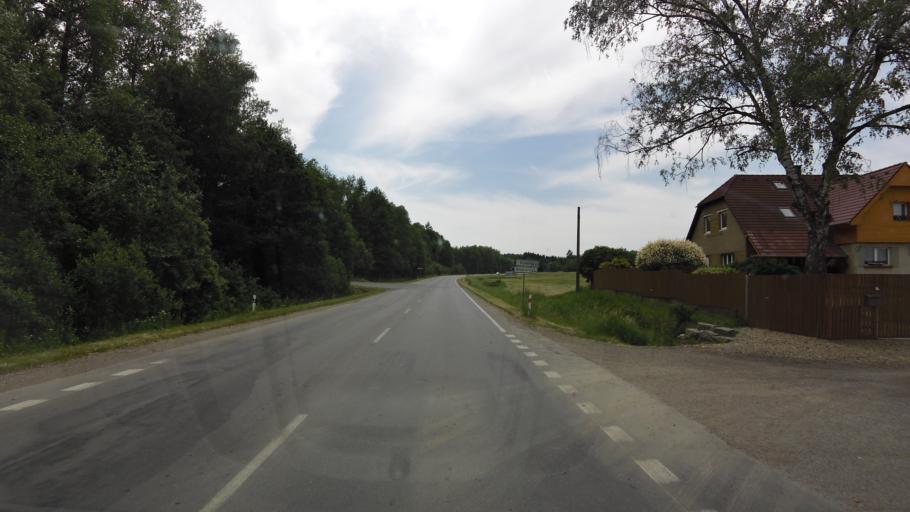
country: CZ
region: Plzensky
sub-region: Okres Rokycany
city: Rokycany
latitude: 49.7236
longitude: 13.5800
